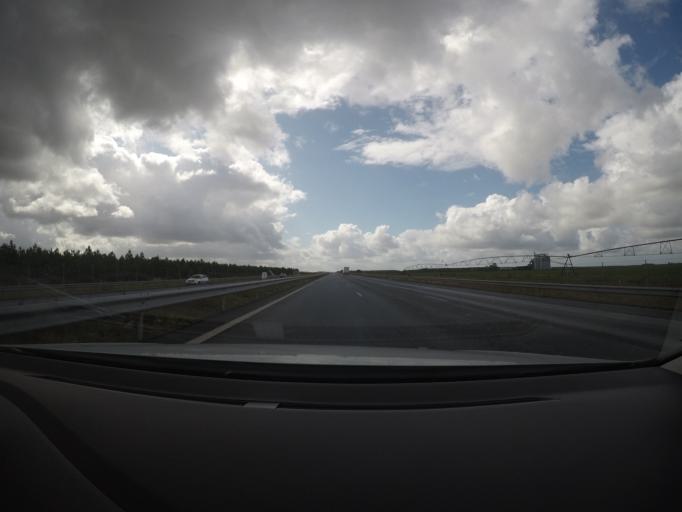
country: FR
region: Aquitaine
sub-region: Departement des Landes
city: Ychoux
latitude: 44.2936
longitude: -0.8879
